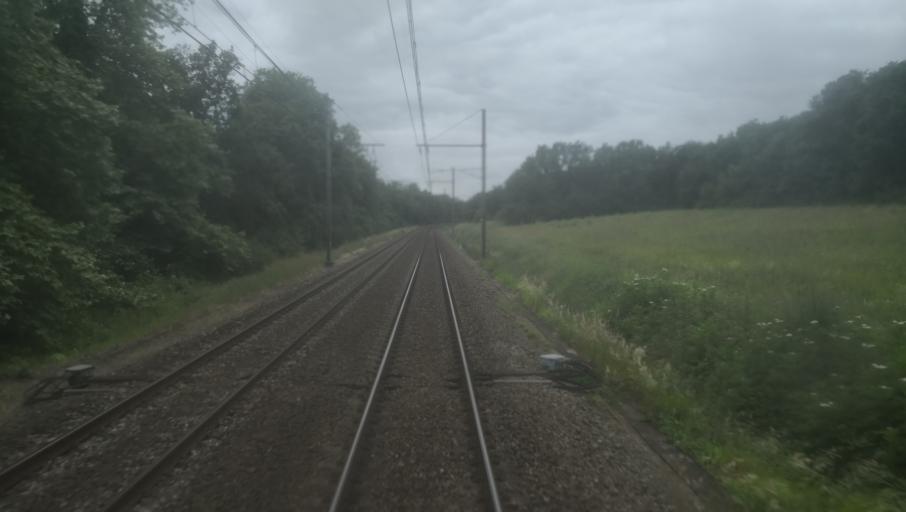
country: FR
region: Midi-Pyrenees
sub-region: Departement du Tarn-et-Garonne
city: Verdun-sur-Garonne
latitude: 43.8684
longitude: 1.2736
